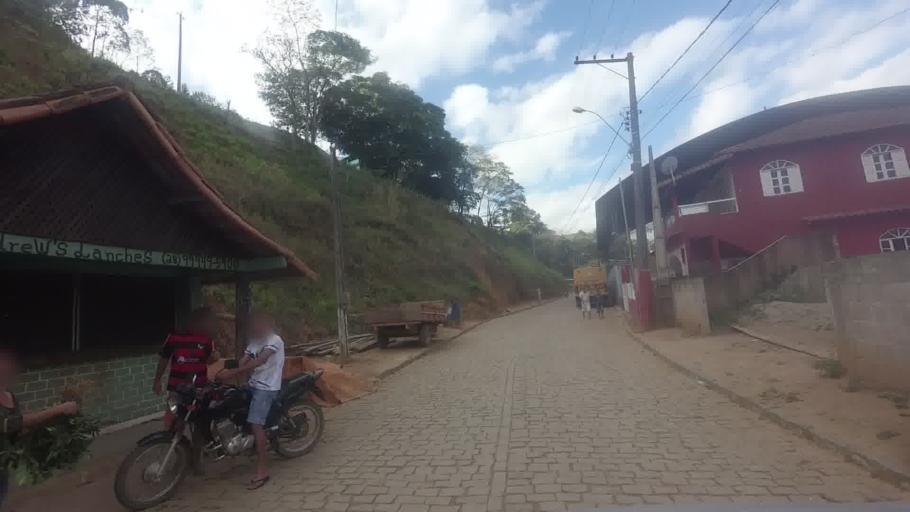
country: BR
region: Espirito Santo
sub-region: Sao Jose Do Calcado
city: Sao Jose do Calcado
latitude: -20.9728
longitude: -41.5092
